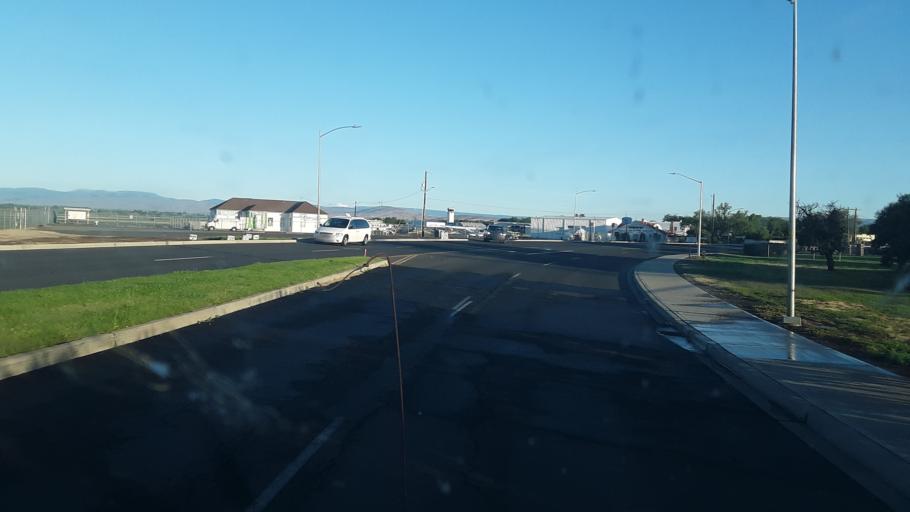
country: US
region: Washington
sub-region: Yakima County
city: Yakima
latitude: 46.5672
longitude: -120.5286
